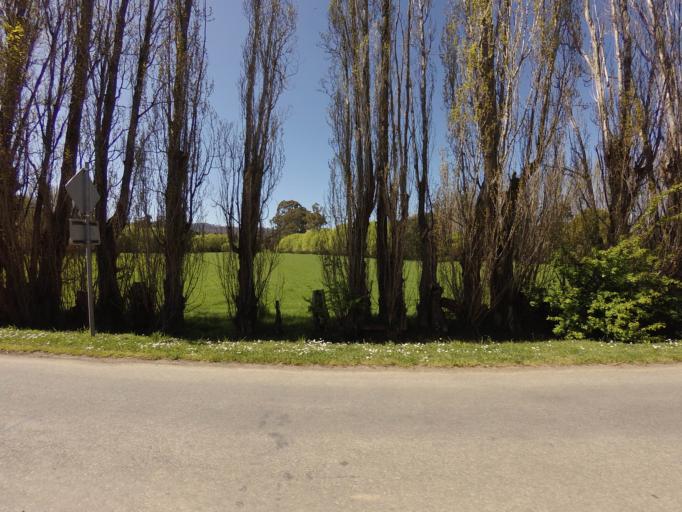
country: AU
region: Tasmania
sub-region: Derwent Valley
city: New Norfolk
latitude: -42.6733
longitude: 146.7897
